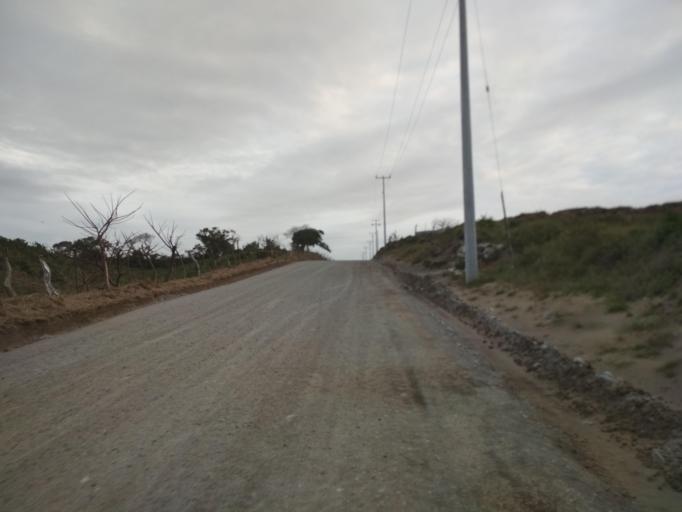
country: MX
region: Veracruz
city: Anton Lizardo
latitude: 19.0471
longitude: -95.9928
